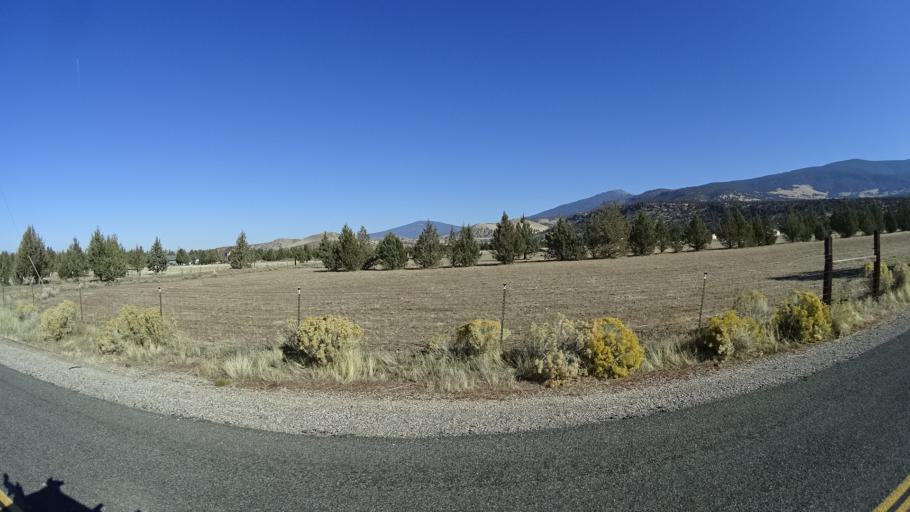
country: US
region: California
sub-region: Siskiyou County
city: Montague
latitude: 41.6427
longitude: -122.3491
